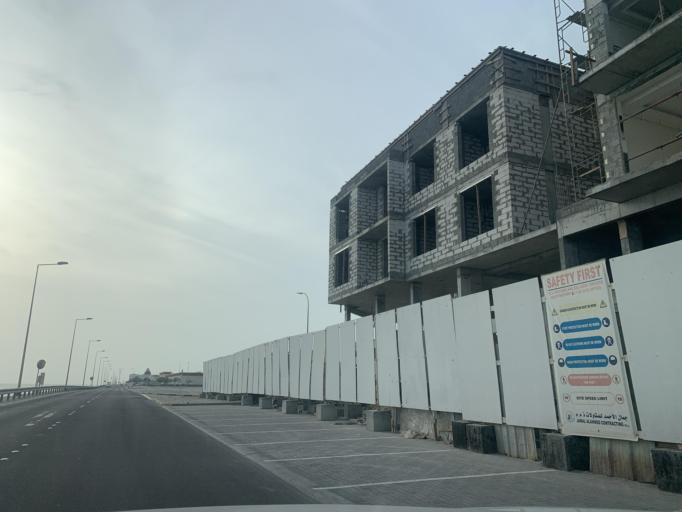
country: BH
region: Muharraq
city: Al Muharraq
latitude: 26.3016
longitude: 50.6298
